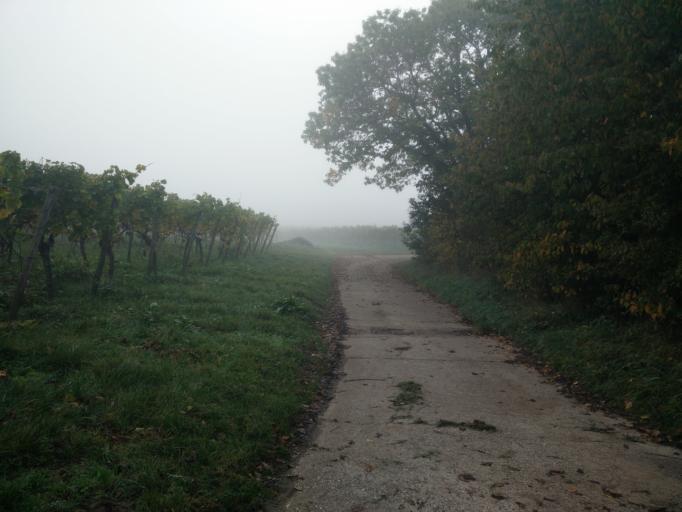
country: DE
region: Rheinland-Pfalz
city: Oberhausen
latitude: 49.1063
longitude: 8.0584
